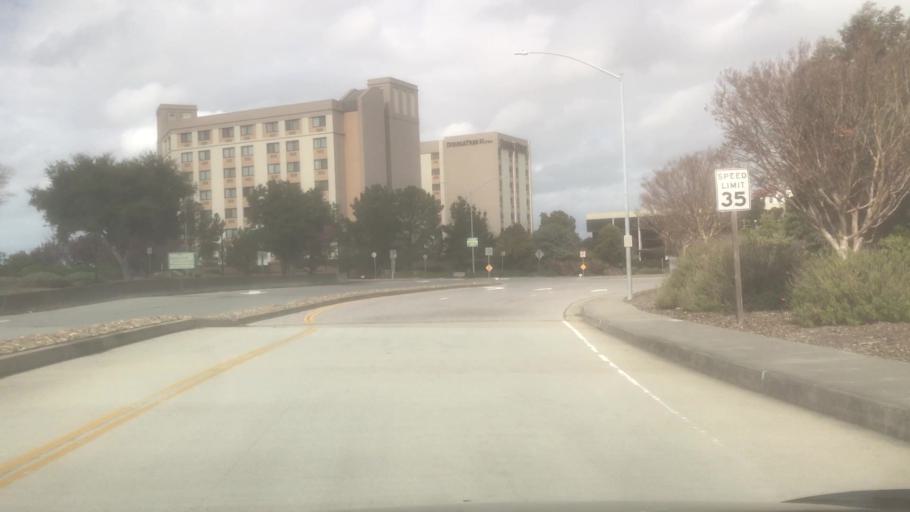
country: US
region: California
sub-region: San Mateo County
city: Burlingame
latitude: 37.5892
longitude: -122.3518
